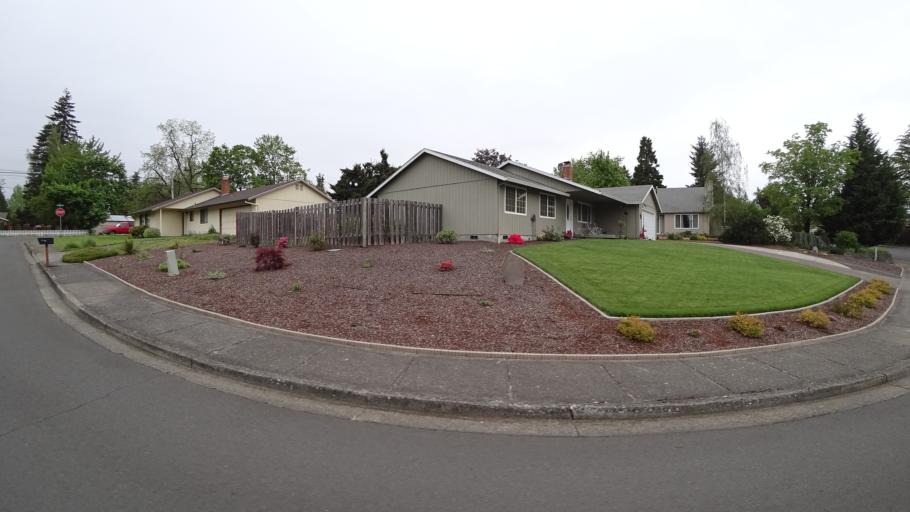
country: US
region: Oregon
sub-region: Washington County
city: Aloha
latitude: 45.5059
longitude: -122.8745
